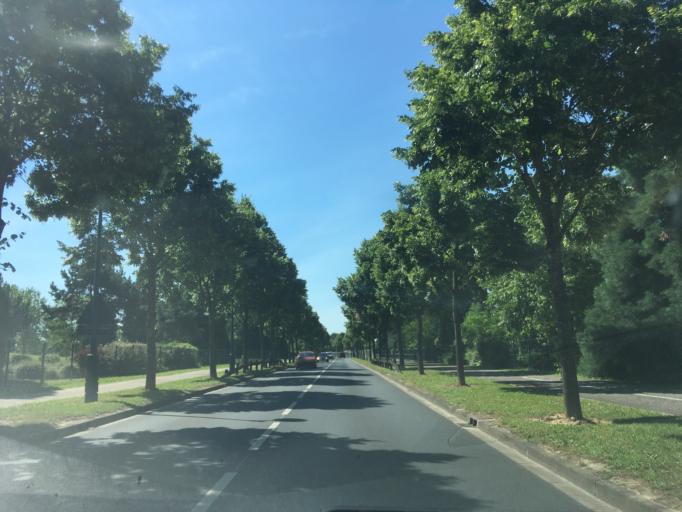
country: FR
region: Ile-de-France
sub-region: Departement de Seine-et-Marne
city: Magny-le-Hongre
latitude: 48.8568
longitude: 2.8148
